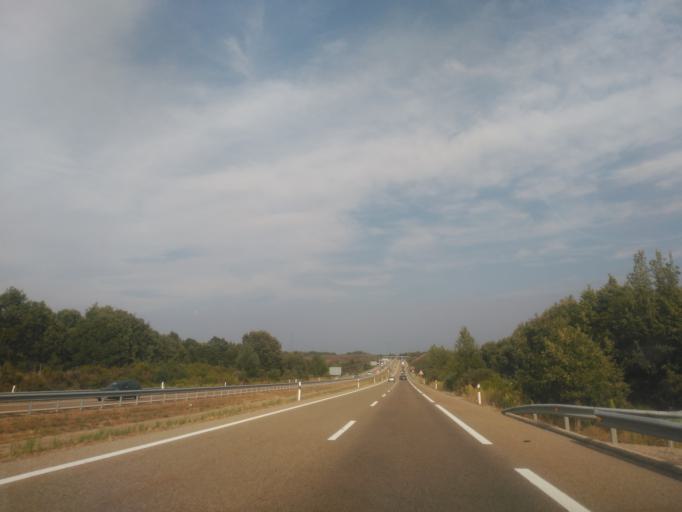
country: ES
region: Castille and Leon
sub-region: Provincia de Zamora
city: Robleda-Cervantes
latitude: 42.0555
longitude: -6.5939
